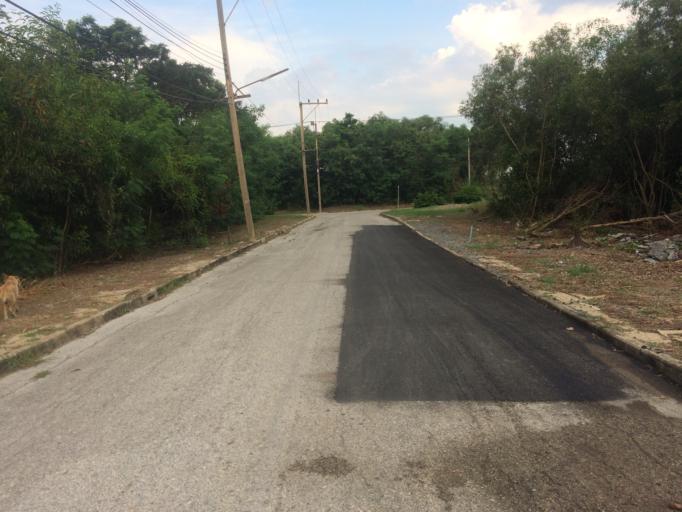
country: TH
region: Pathum Thani
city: Khlong Luang
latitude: 14.0518
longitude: 100.5976
